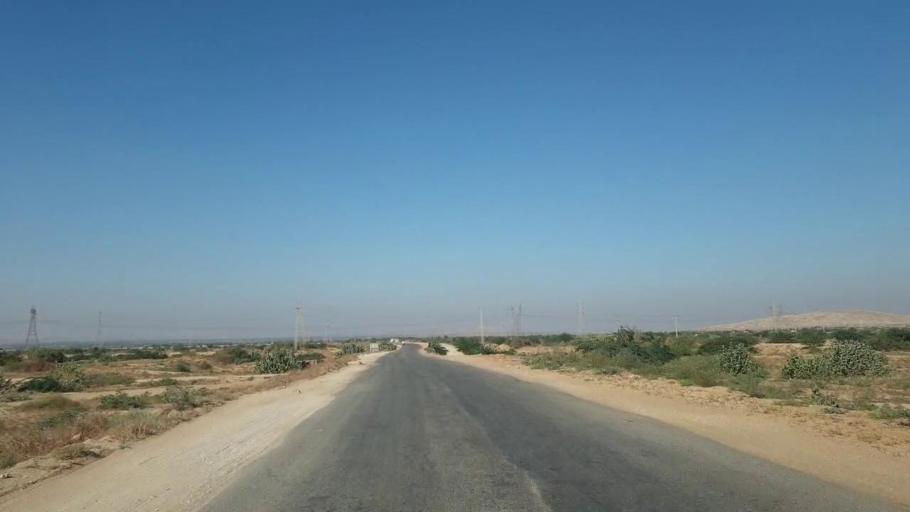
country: PK
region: Sindh
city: Gharo
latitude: 25.1702
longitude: 67.6601
